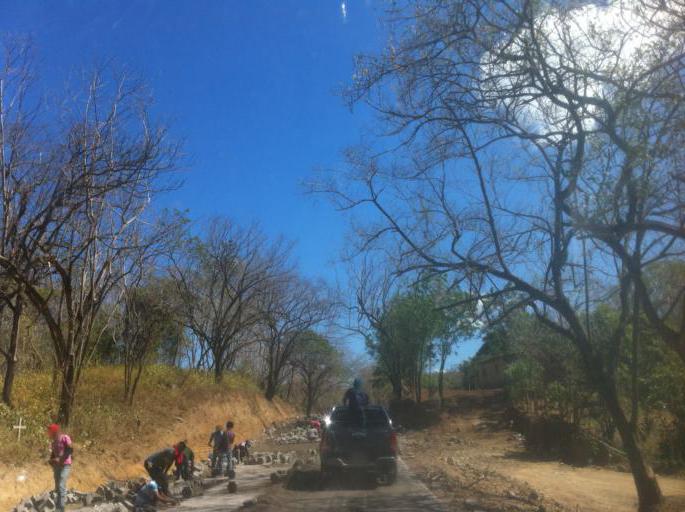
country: NI
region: Rivas
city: Tola
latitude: 11.3984
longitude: -85.9932
